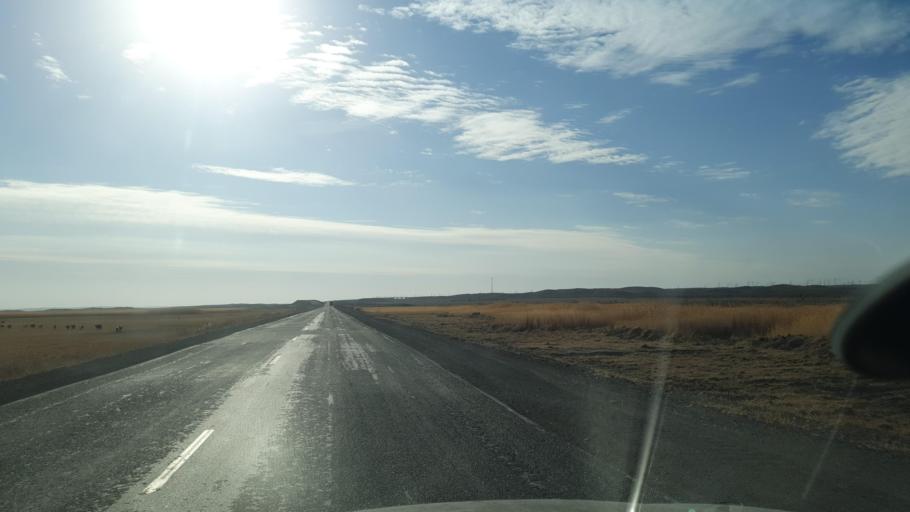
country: KZ
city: Priozersk
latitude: 45.8364
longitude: 73.4550
